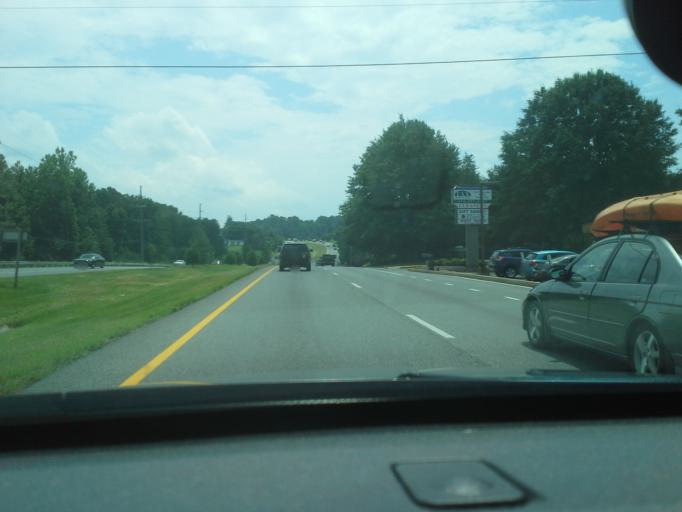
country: US
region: Maryland
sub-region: Calvert County
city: Dunkirk Town Center
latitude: 38.6900
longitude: -76.6388
